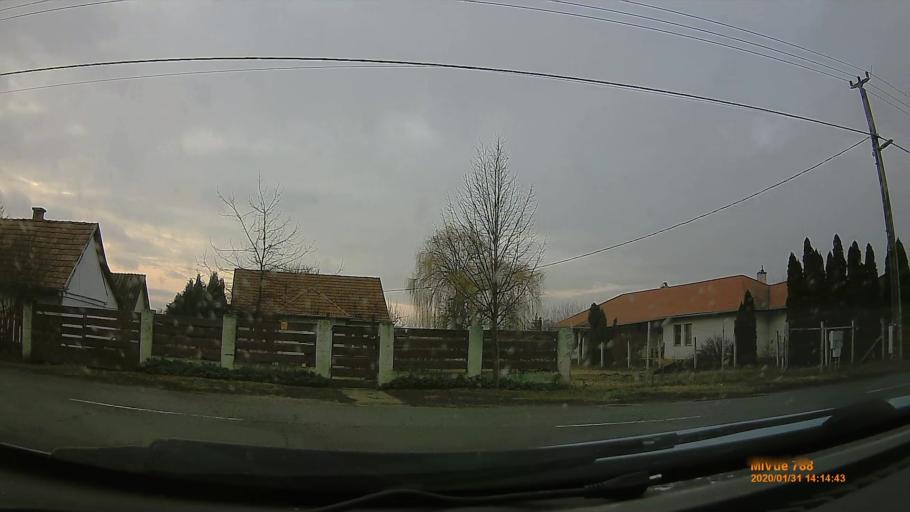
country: HU
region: Szabolcs-Szatmar-Bereg
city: Nyiregyhaza
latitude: 47.9536
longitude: 21.6763
